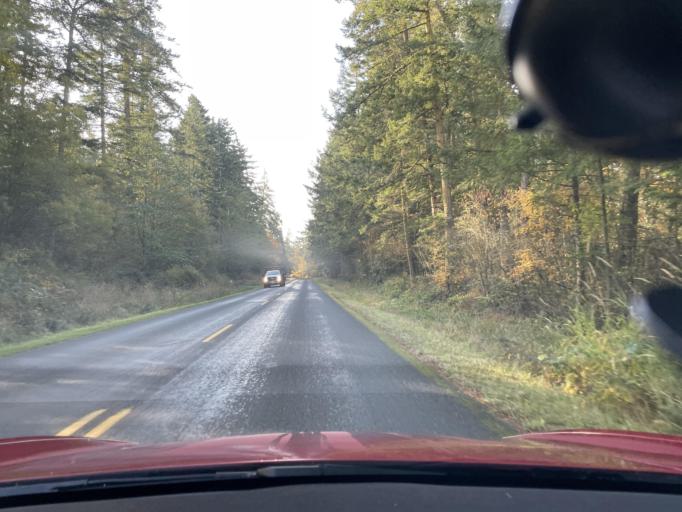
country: US
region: Washington
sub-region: San Juan County
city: Friday Harbor
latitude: 48.5537
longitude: -123.1646
